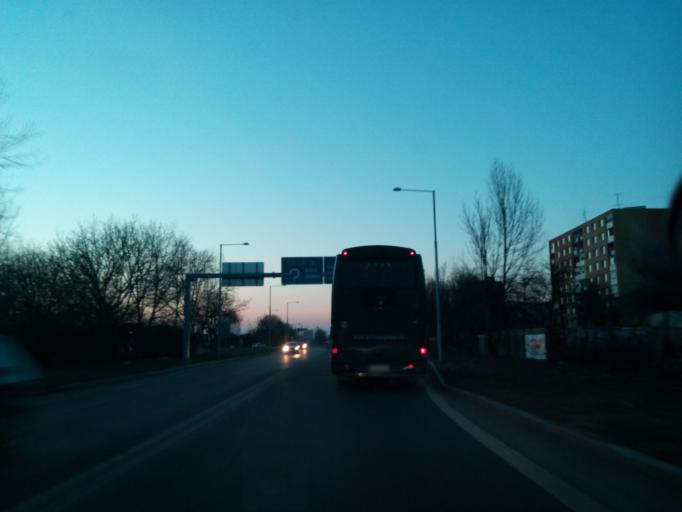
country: SK
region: Kosicky
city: Michalovce
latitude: 48.7480
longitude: 21.9077
